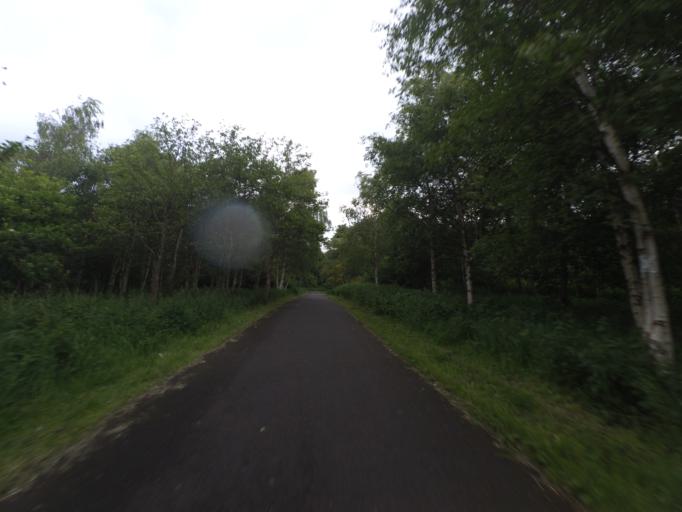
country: GB
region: Scotland
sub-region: West Lothian
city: Seafield
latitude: 55.9290
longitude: -3.1494
